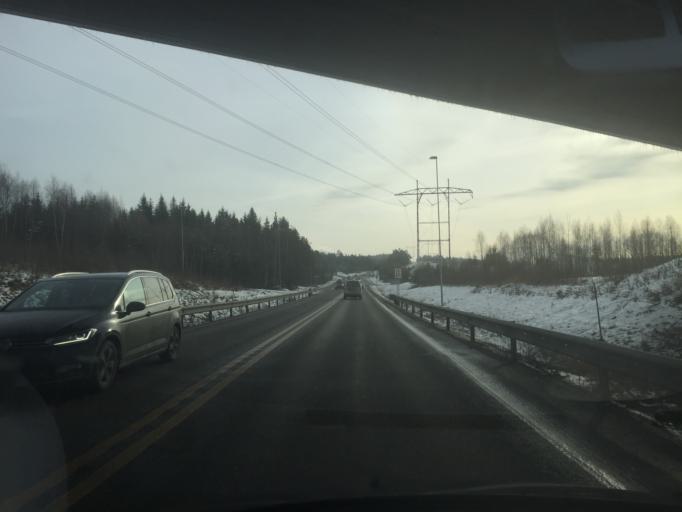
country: NO
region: Hedmark
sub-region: Loten
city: Loten
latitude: 60.7870
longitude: 11.3023
